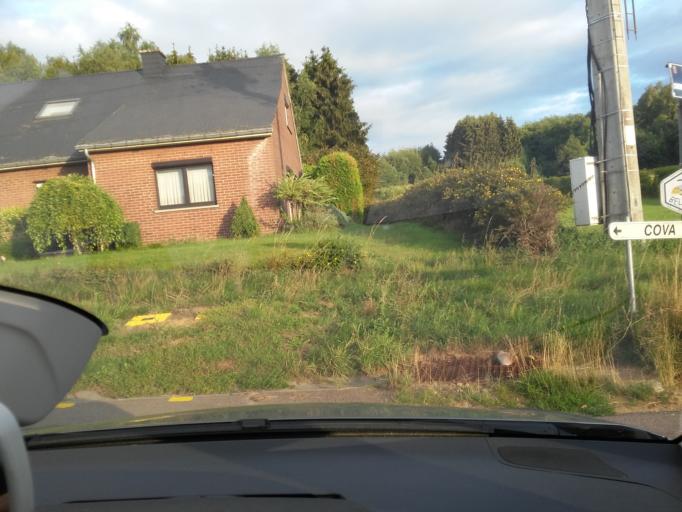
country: BE
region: Wallonia
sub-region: Province du Luxembourg
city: Arlon
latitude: 49.6985
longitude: 5.8127
